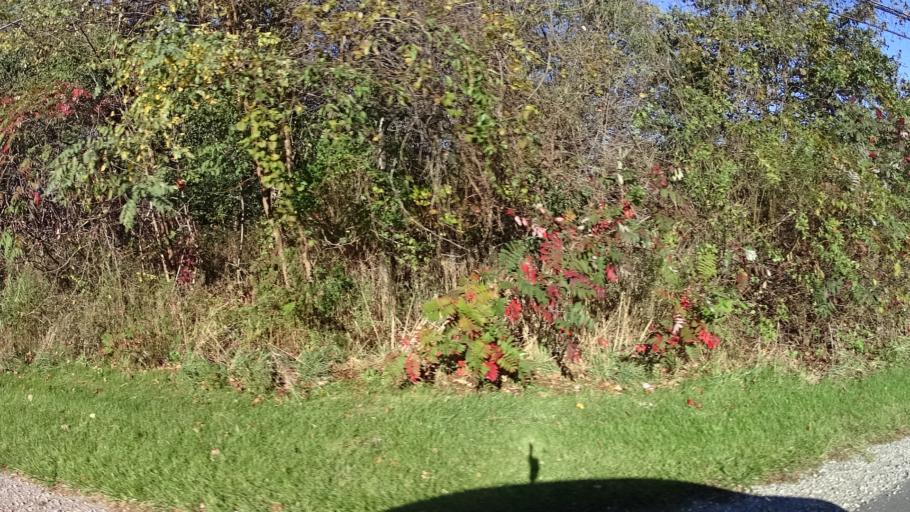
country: US
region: Ohio
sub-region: Lorain County
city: South Amherst
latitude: 41.3536
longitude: -82.2583
